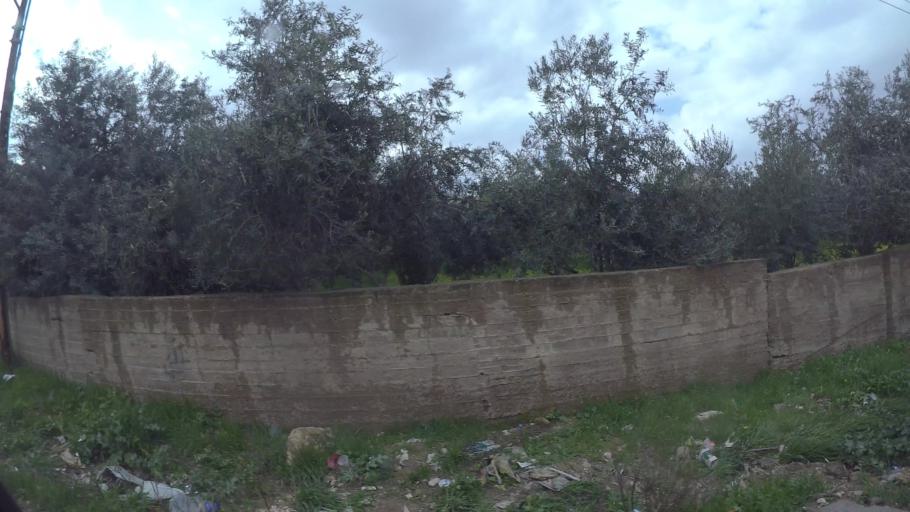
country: JO
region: Amman
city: Al Jubayhah
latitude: 32.0507
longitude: 35.8417
